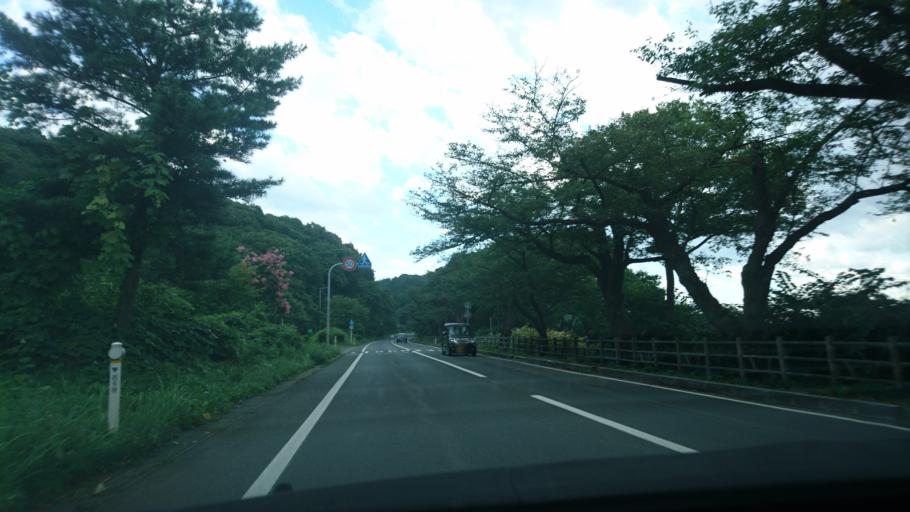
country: JP
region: Iwate
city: Kitakami
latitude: 39.2698
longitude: 141.1255
